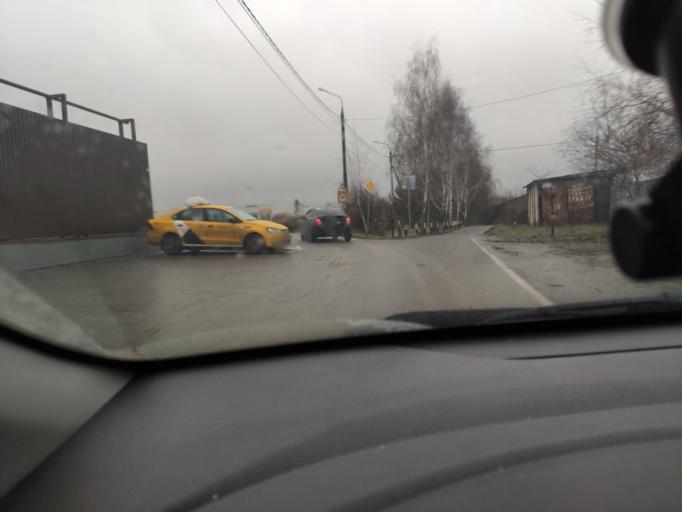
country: RU
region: Moscow
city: Zagor'ye
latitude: 55.5658
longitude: 37.6632
